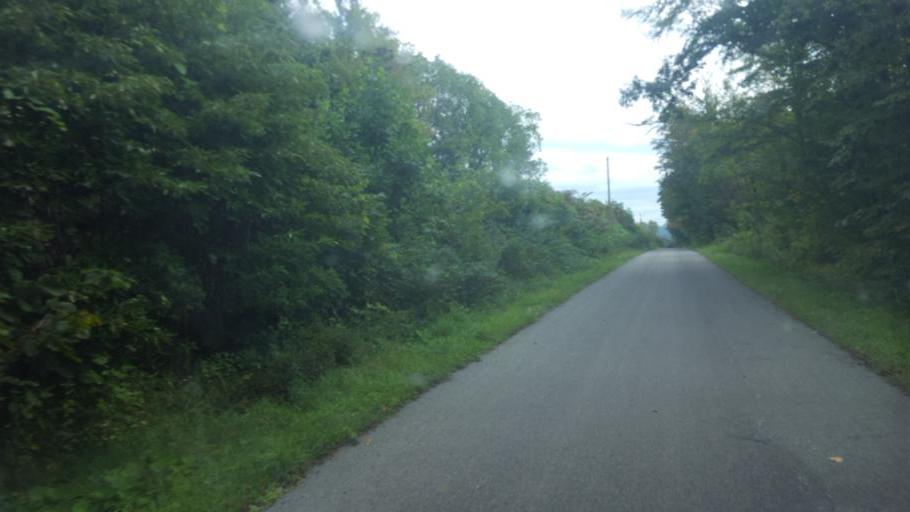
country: US
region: Pennsylvania
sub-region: Mercer County
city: Greenville
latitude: 41.5161
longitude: -80.3879
